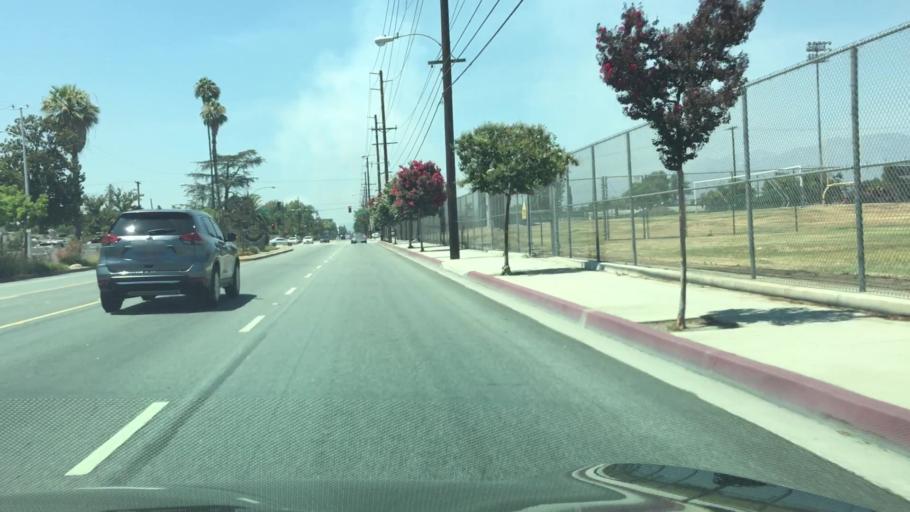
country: US
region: California
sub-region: Los Angeles County
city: West Puente Valley
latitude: 34.0497
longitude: -117.9804
